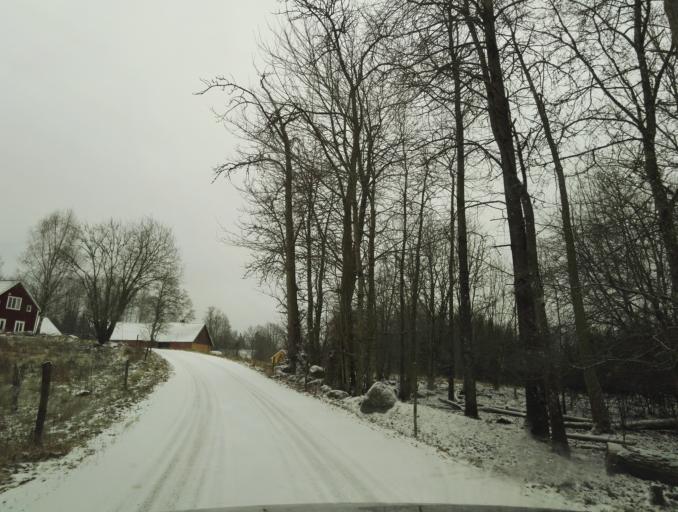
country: SE
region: Kronoberg
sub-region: Alvesta Kommun
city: Vislanda
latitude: 56.7042
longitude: 14.4163
